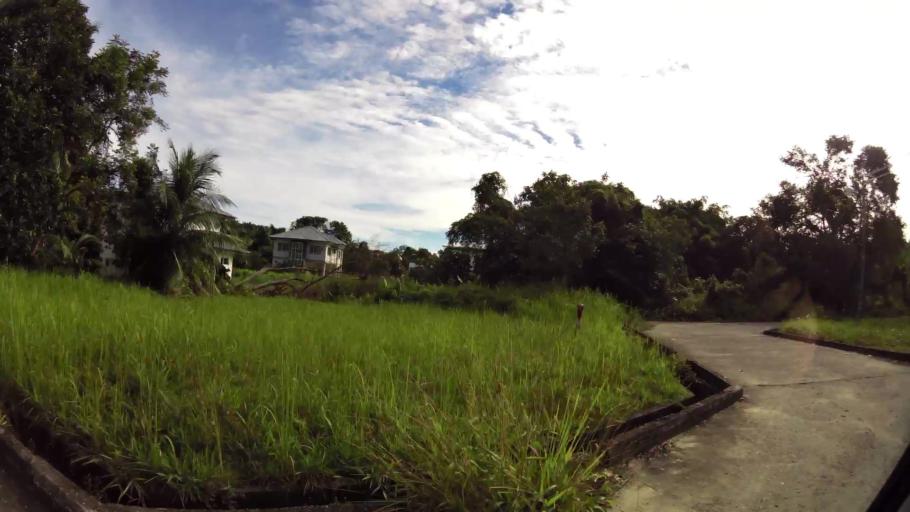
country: BN
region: Brunei and Muara
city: Bandar Seri Begawan
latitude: 4.8931
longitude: 114.9664
